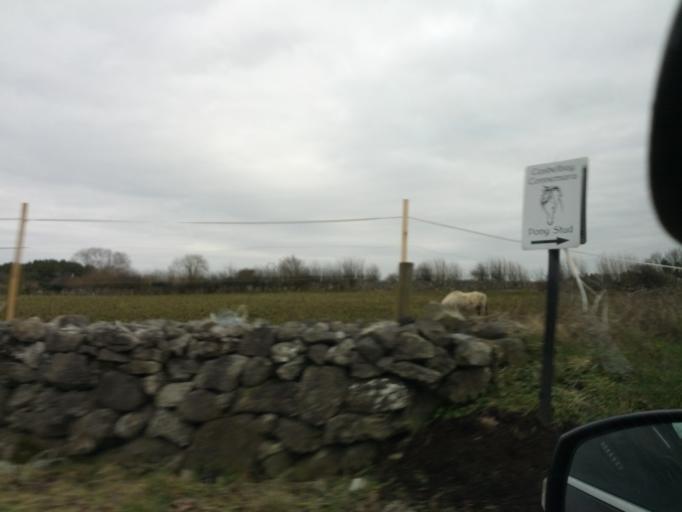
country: IE
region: Connaught
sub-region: County Galway
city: Athenry
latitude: 53.2699
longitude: -8.7431
